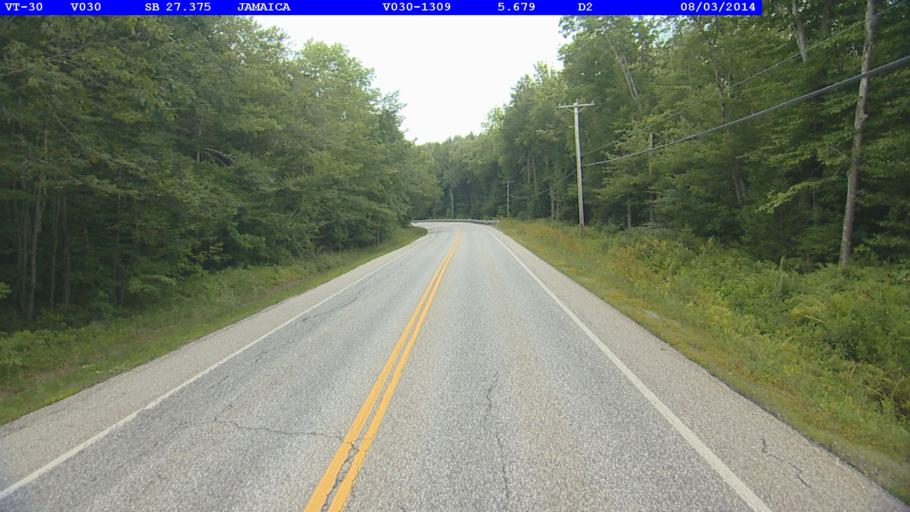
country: US
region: Vermont
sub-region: Windham County
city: Dover
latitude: 43.1145
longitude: -72.8026
